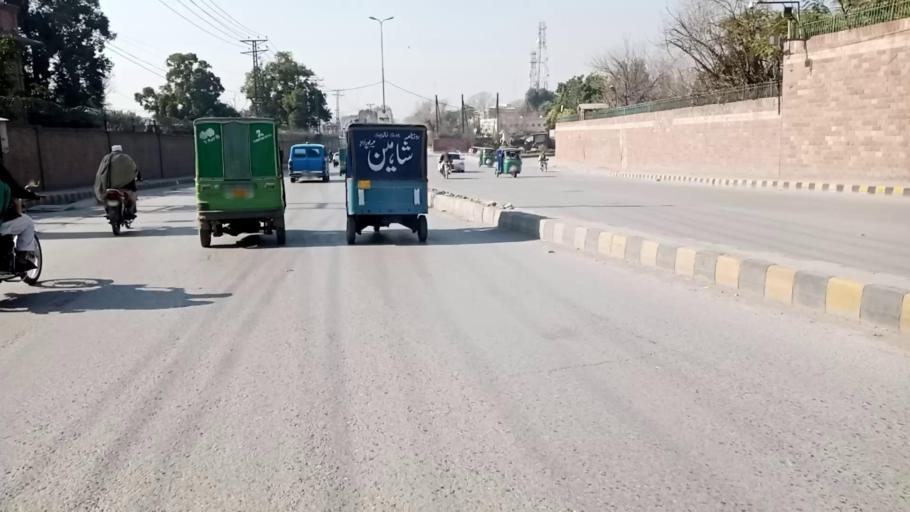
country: PK
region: Khyber Pakhtunkhwa
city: Peshawar
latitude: 34.0077
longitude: 71.5573
